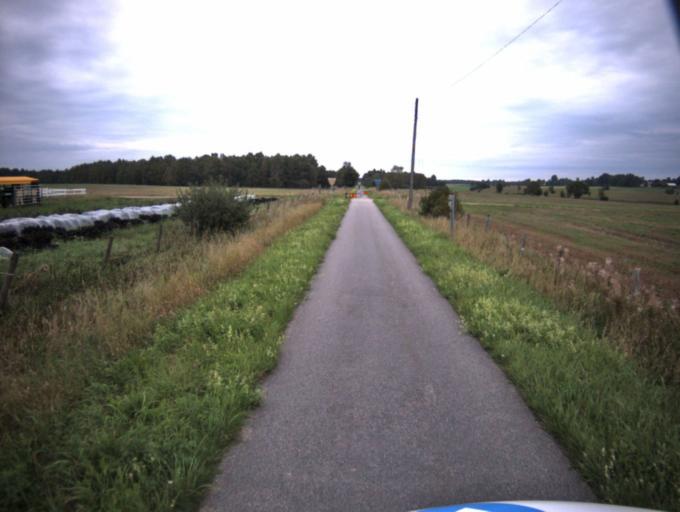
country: SE
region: Vaestra Goetaland
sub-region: Ulricehamns Kommun
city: Ulricehamn
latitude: 57.9554
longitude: 13.5091
